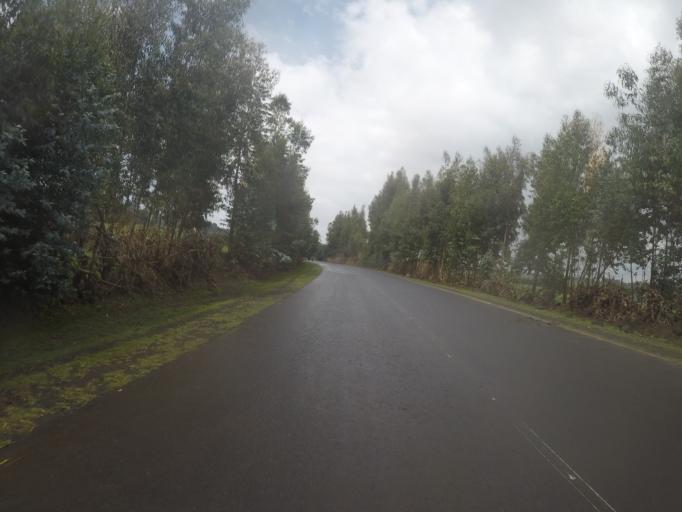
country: ET
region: Amhara
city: Debark'
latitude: 13.1120
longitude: 37.8666
